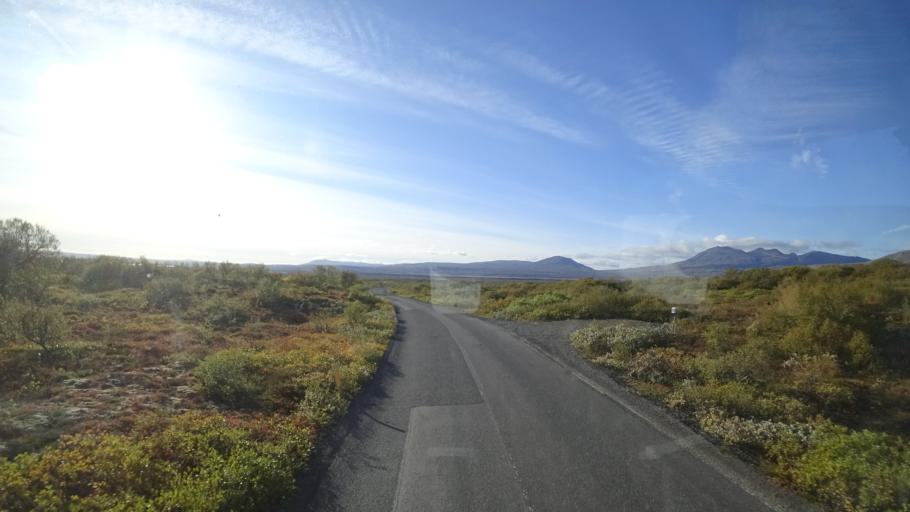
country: IS
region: South
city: Hveragerdi
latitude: 64.2581
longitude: -21.0314
